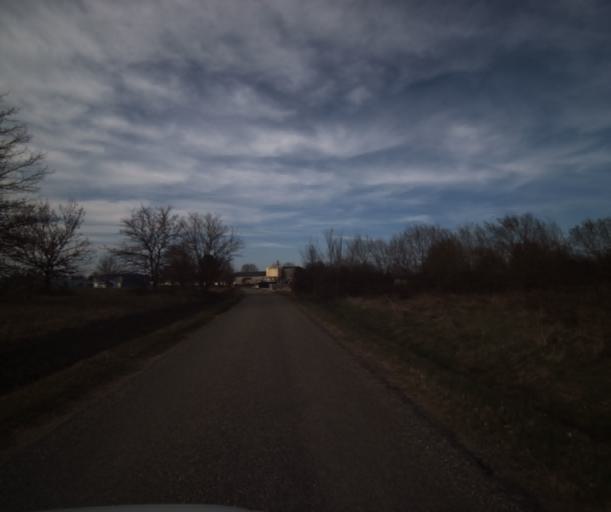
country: FR
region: Midi-Pyrenees
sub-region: Departement du Tarn-et-Garonne
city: Labastide-Saint-Pierre
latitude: 43.9125
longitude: 1.3738
